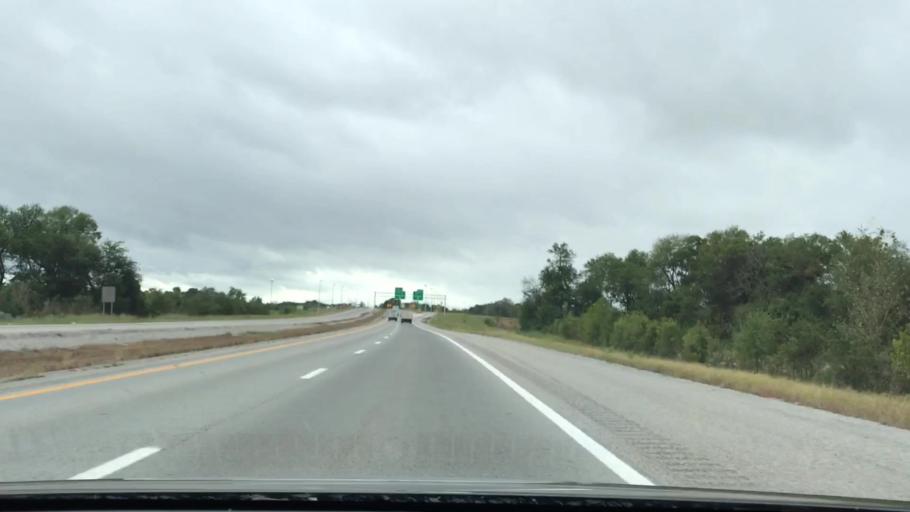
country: US
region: Kentucky
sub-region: Christian County
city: Fort Campbell North
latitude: 36.7518
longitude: -87.5088
